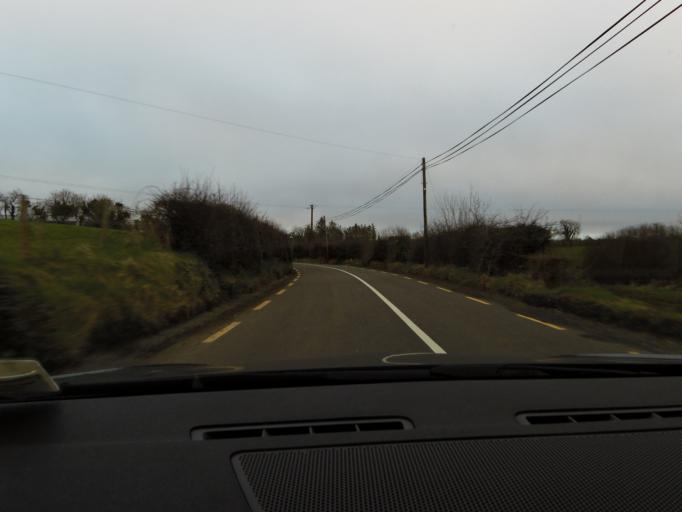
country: IE
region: Connaught
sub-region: Sligo
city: Ballymote
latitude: 54.0045
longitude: -8.5426
